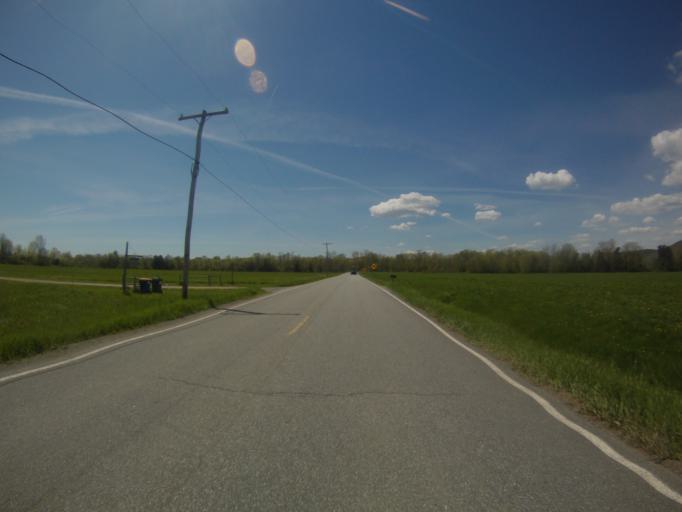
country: US
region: New York
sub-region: Essex County
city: Port Henry
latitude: 43.9884
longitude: -73.4239
